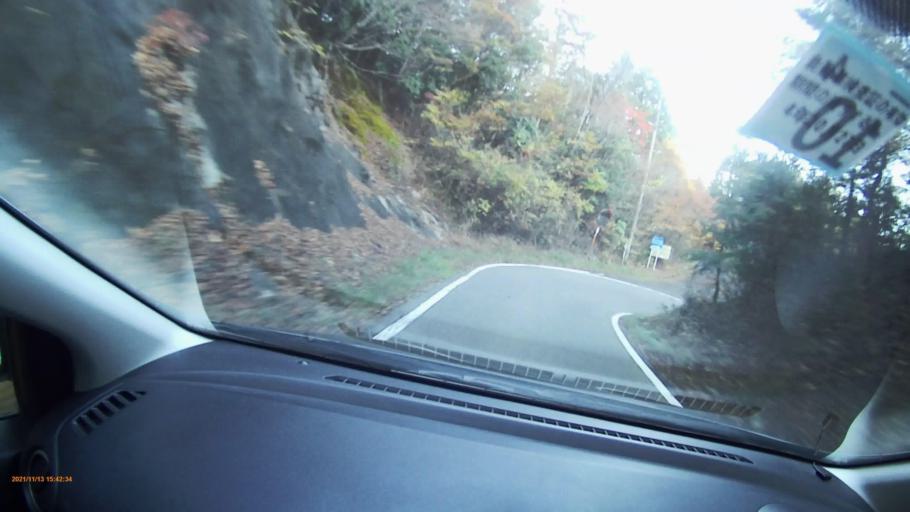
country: JP
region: Gifu
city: Nakatsugawa
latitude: 35.5927
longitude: 137.3926
